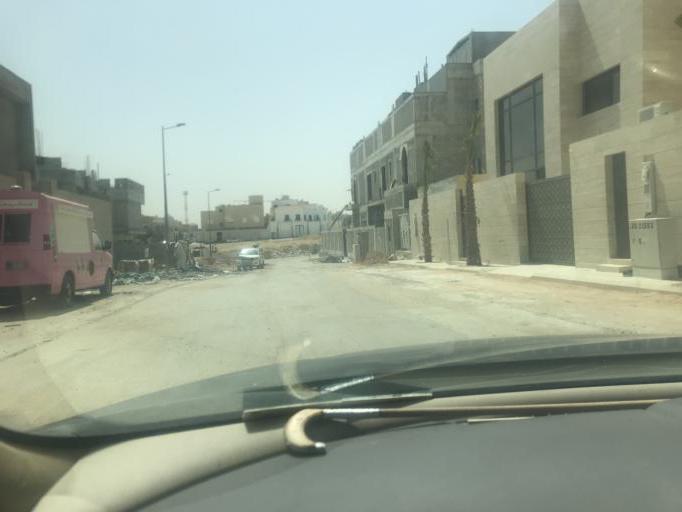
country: SA
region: Ar Riyad
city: Riyadh
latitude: 24.7867
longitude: 46.5820
